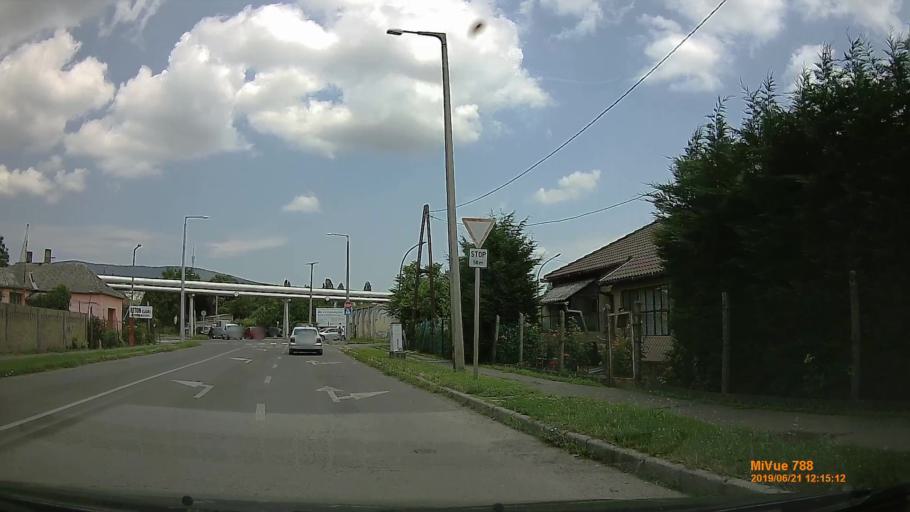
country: HU
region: Baranya
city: Pecs
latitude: 46.0620
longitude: 18.2132
